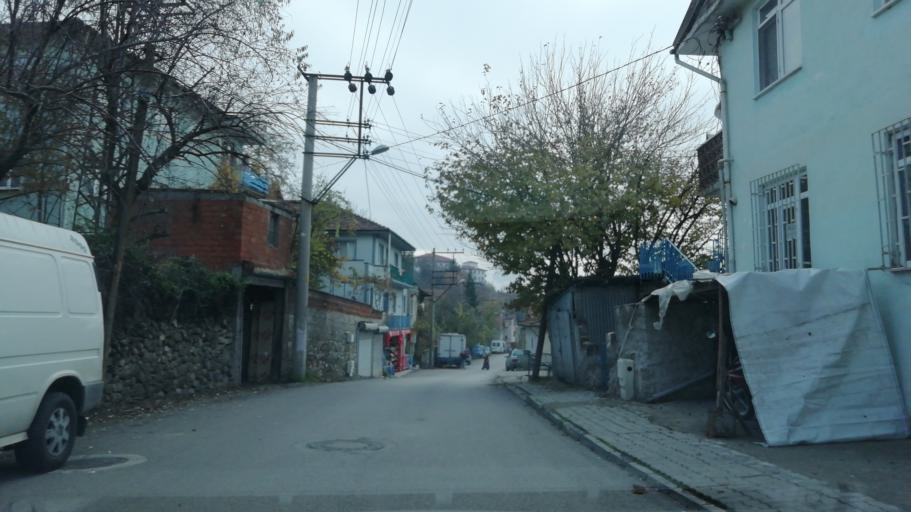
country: TR
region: Karabuk
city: Karabuk
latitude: 41.2139
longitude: 32.6286
